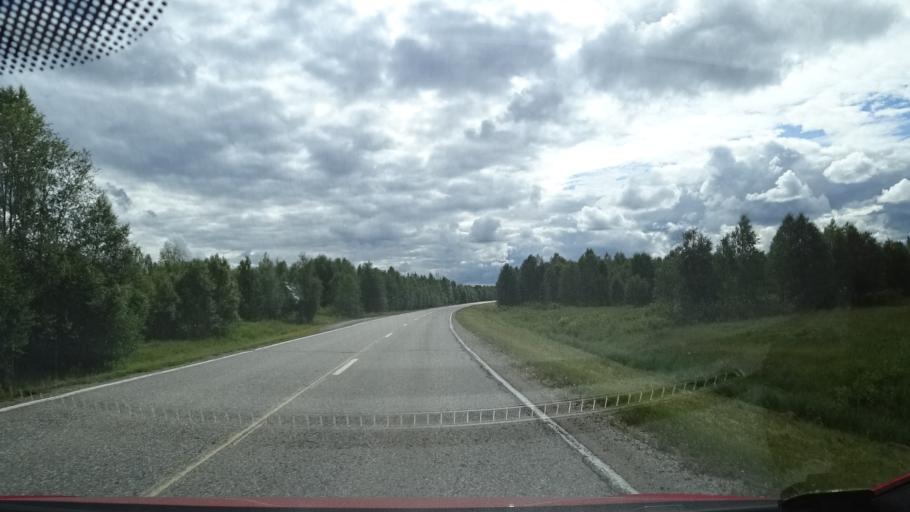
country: FI
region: Lapland
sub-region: Tunturi-Lappi
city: Kittilae
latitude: 67.4661
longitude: 24.9488
